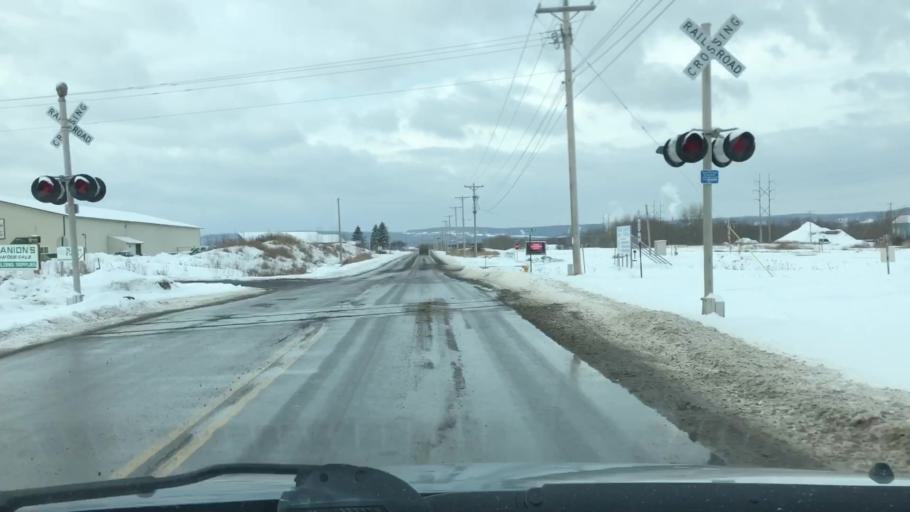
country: US
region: Wisconsin
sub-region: Douglas County
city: Superior
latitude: 46.7280
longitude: -92.1153
